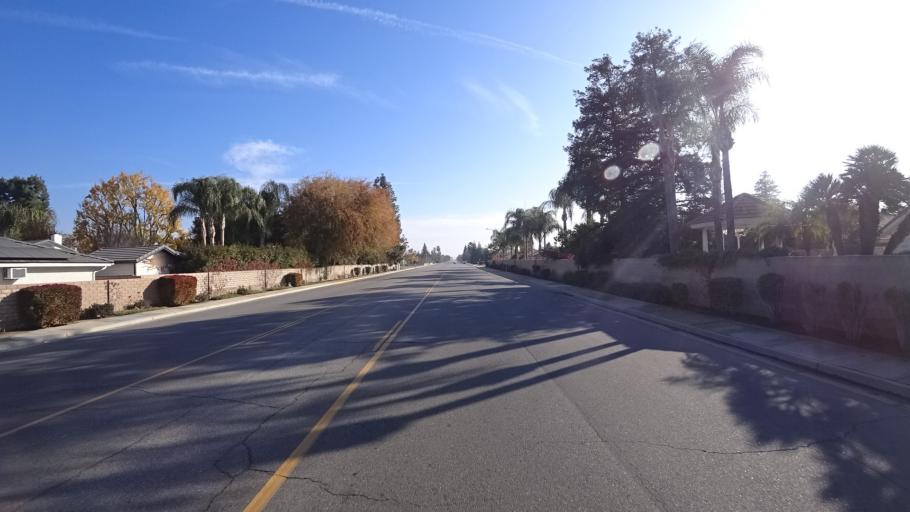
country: US
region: California
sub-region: Kern County
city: Greenacres
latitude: 35.4199
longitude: -119.0892
